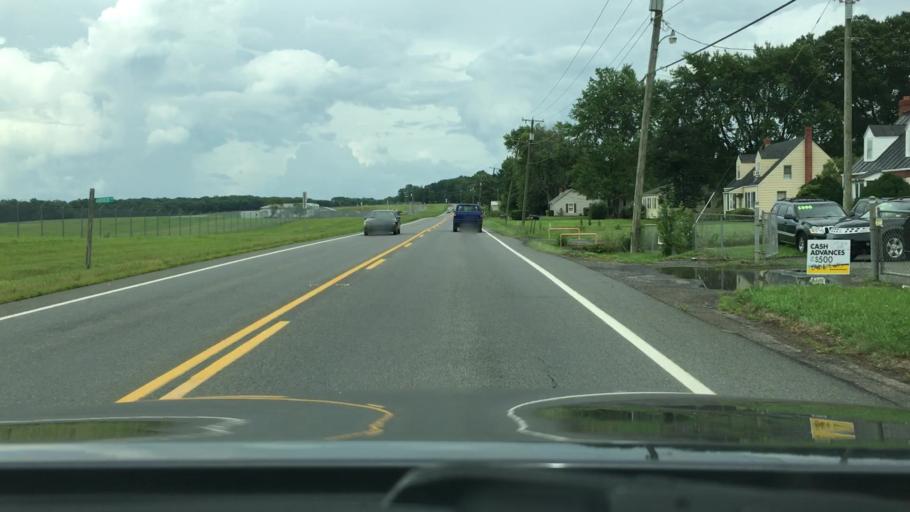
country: US
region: Virginia
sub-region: Orange County
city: Orange
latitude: 38.2452
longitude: -78.0478
